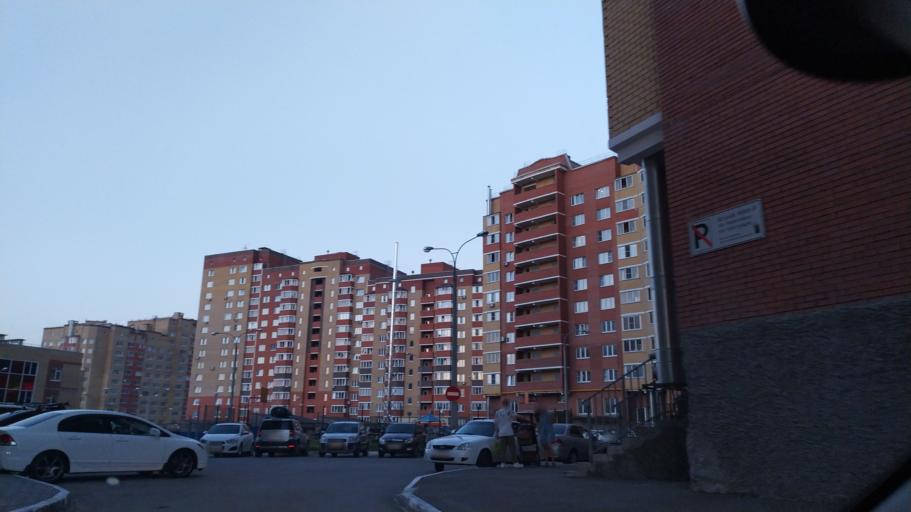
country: RU
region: Chuvashia
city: Novyye Lapsary
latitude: 56.1329
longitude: 47.1490
